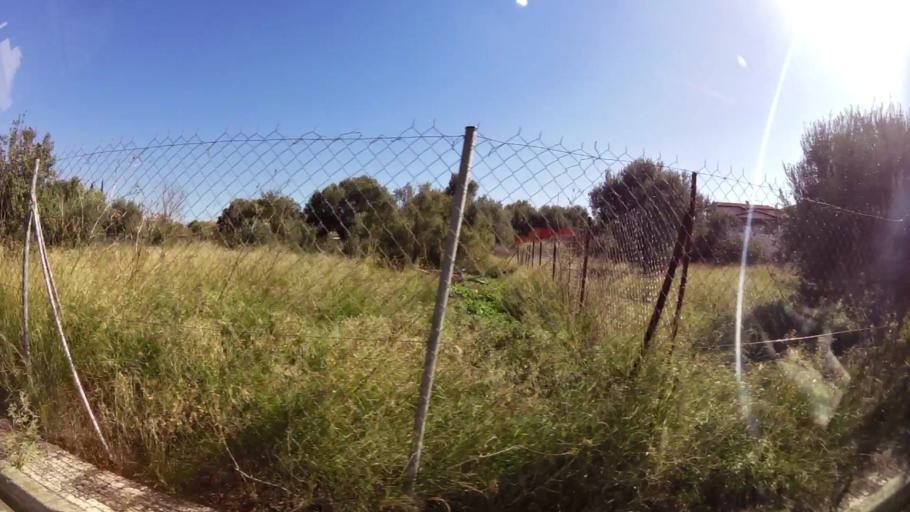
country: GR
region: Attica
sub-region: Nomarchia Athinas
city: Kifisia
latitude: 38.0852
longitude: 23.7977
